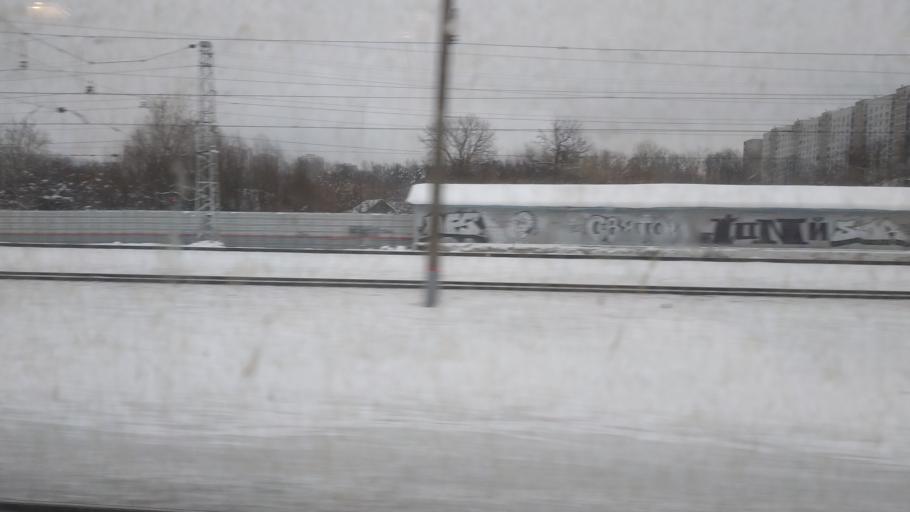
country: RU
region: Moskovskaya
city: Shcherbinka
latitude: 55.5433
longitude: 37.5711
